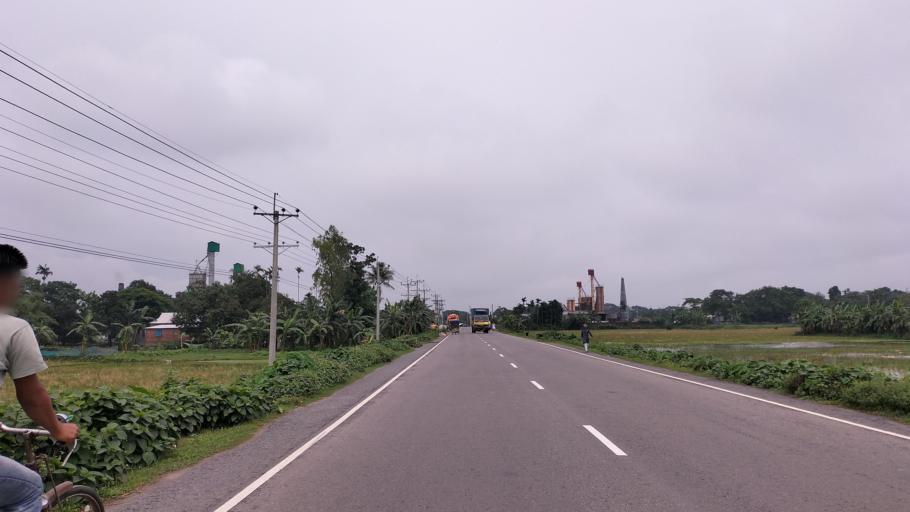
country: BD
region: Dhaka
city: Netrakona
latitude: 24.8526
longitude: 90.6520
